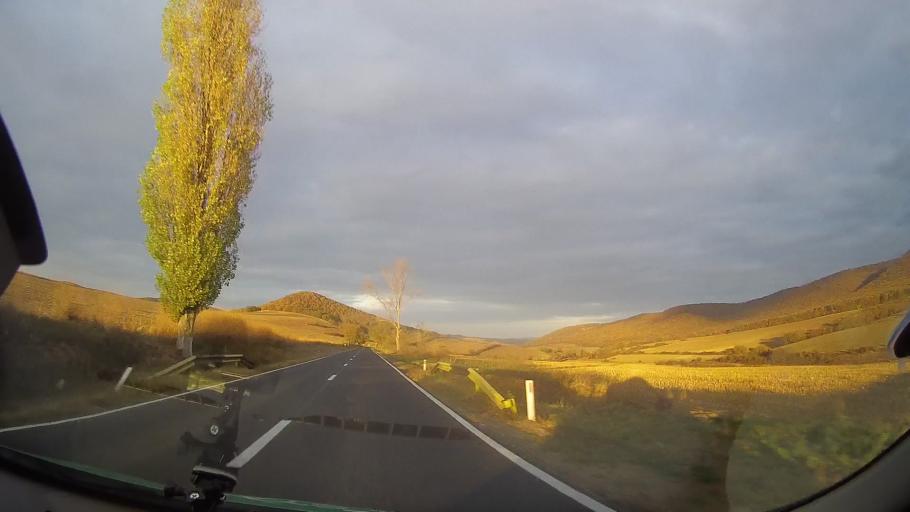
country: RO
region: Tulcea
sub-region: Comuna Ciucurova
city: Ciucurova
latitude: 44.9424
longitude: 28.4945
